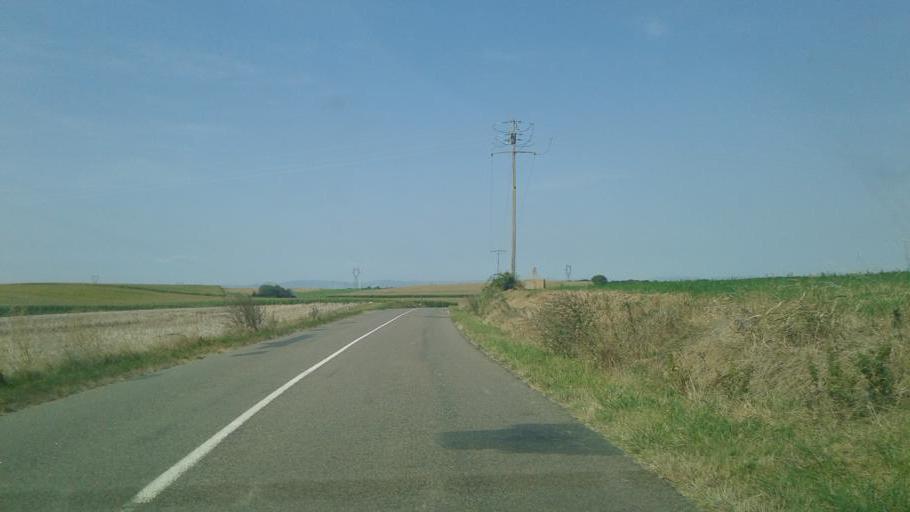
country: FR
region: Rhone-Alpes
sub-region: Departement de l'Ain
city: Beynost
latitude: 45.8582
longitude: 5.0121
